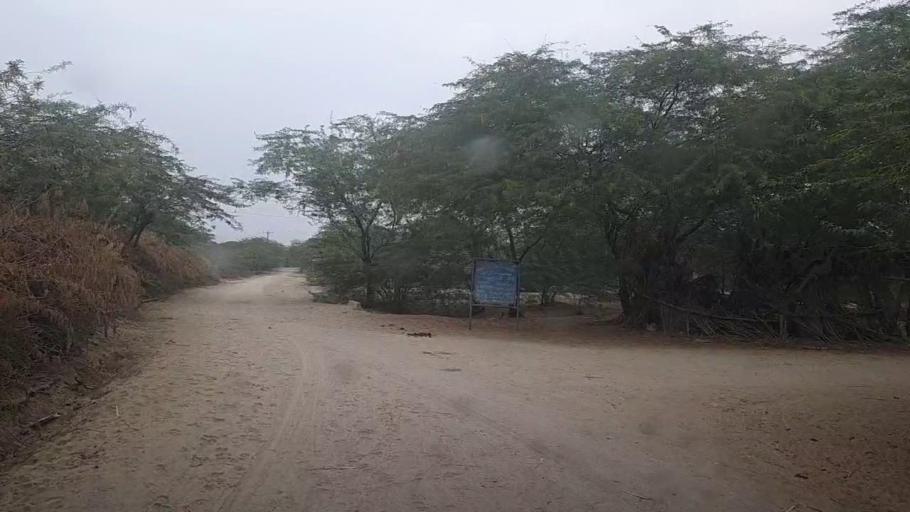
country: PK
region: Sindh
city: Gambat
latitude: 27.3484
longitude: 68.6019
